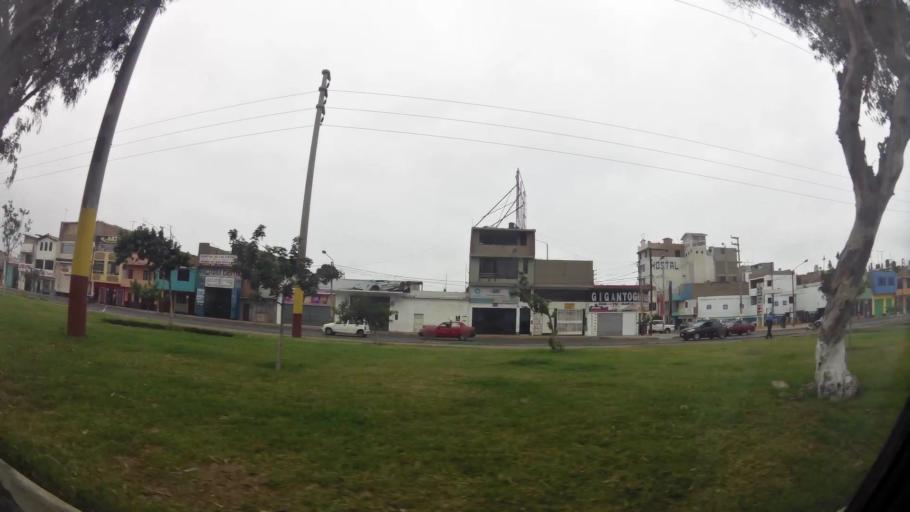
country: PE
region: Ancash
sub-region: Provincia de Santa
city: Chimbote
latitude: -9.0784
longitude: -78.5816
